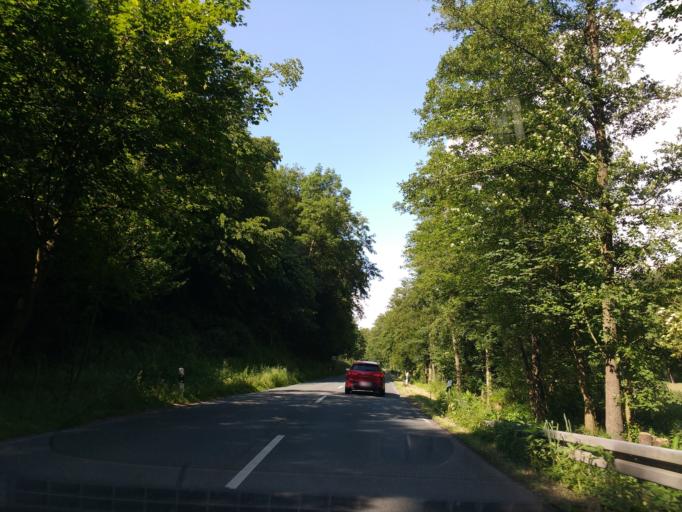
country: DE
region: North Rhine-Westphalia
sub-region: Regierungsbezirk Detmold
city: Vlotho
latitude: 52.1303
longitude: 8.9430
